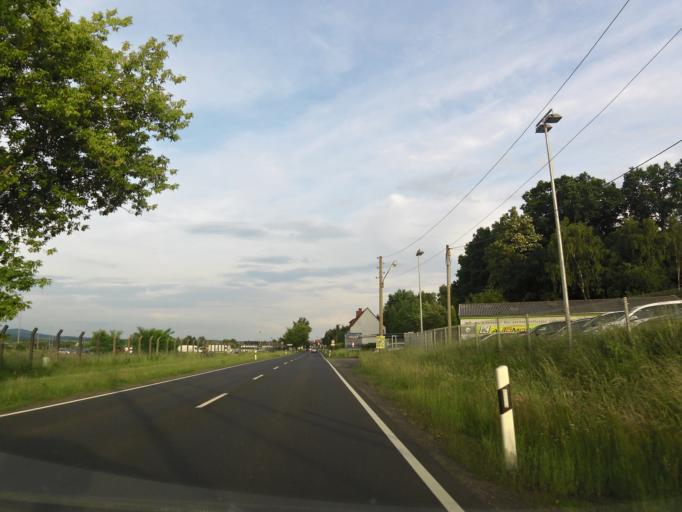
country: DE
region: Thuringia
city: Immelborn
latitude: 50.7991
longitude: 10.2700
